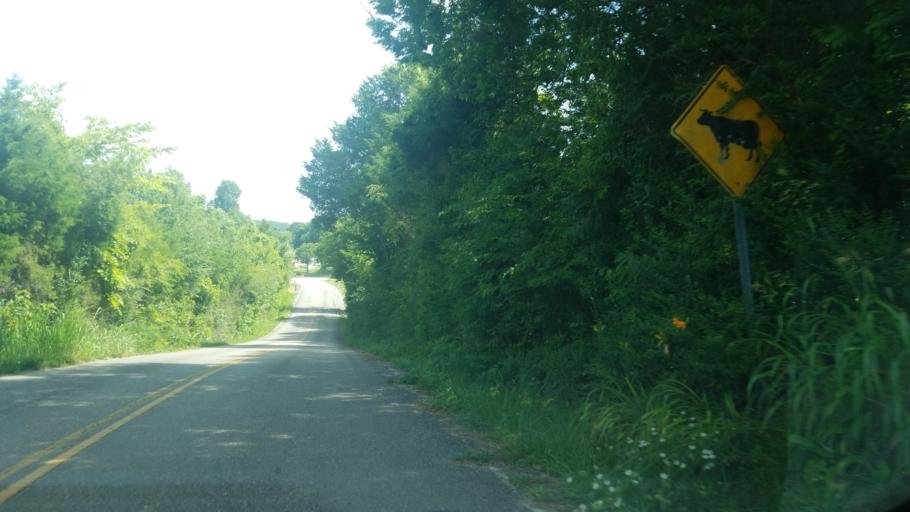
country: US
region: Tennessee
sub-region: Hamilton County
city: Lakesite
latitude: 35.2347
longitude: -85.0141
